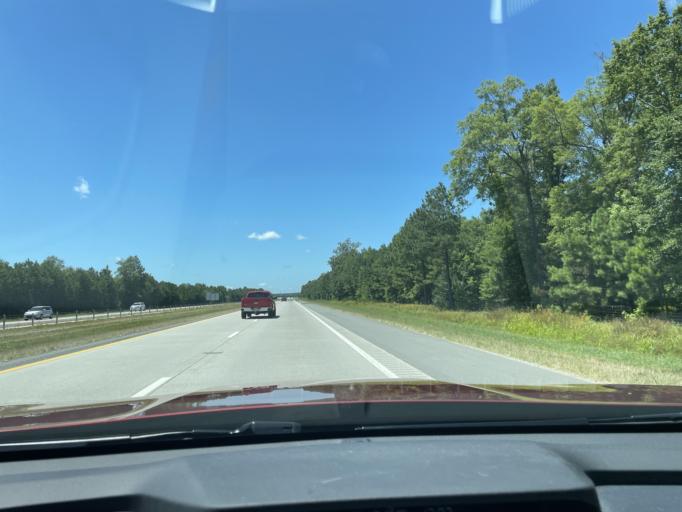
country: US
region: Arkansas
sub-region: Jefferson County
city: Pine Bluff
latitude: 34.1886
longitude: -91.9811
